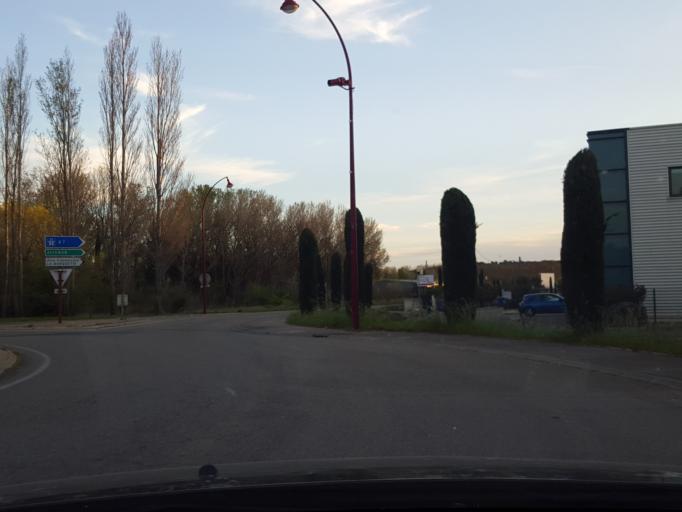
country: FR
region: Provence-Alpes-Cote d'Azur
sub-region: Departement du Vaucluse
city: Entraigues-sur-la-Sorgue
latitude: 43.9946
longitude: 4.9125
